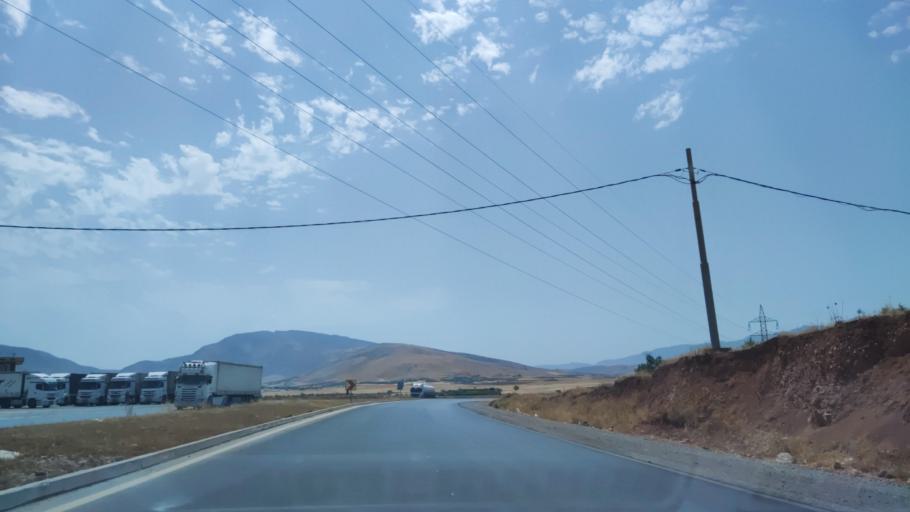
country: IQ
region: Arbil
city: Shaqlawah
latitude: 36.4876
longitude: 44.3804
